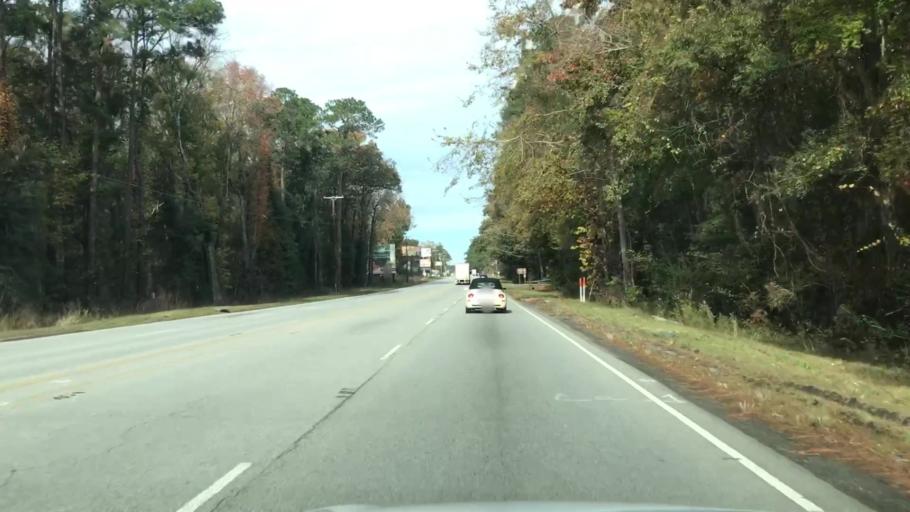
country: US
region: South Carolina
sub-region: Charleston County
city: Ravenel
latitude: 32.7681
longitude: -80.4514
